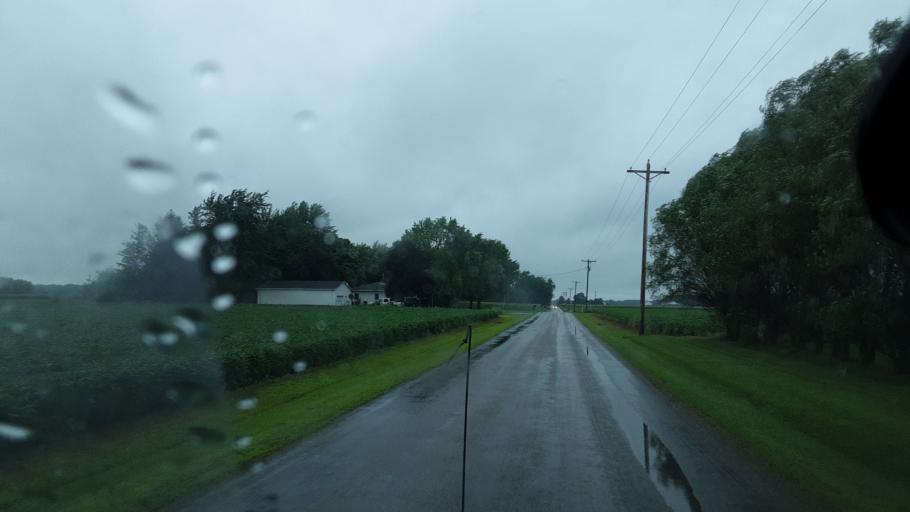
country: US
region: Indiana
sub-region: Adams County
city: Decatur
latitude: 40.7415
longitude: -84.8555
